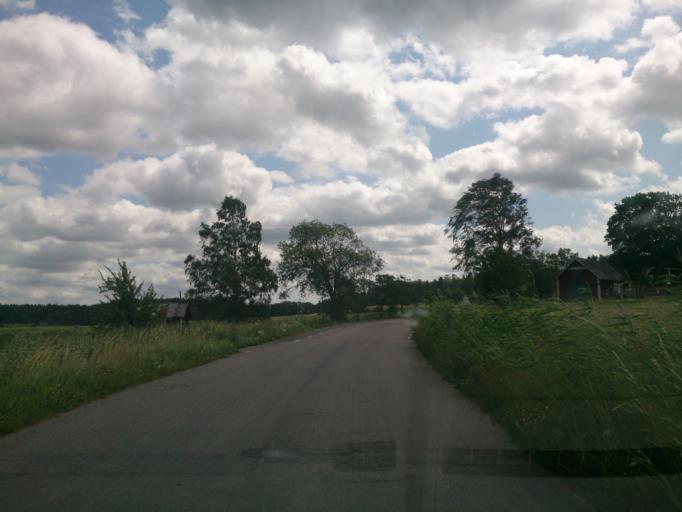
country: SE
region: OEstergoetland
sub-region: Norrkopings Kommun
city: Krokek
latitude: 58.5089
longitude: 16.5368
